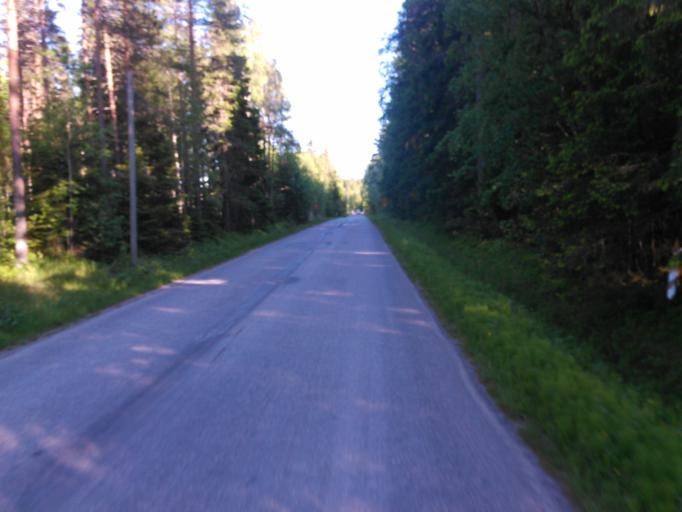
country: SE
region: Vaesterbotten
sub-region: Umea Kommun
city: Ersmark
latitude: 63.8712
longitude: 20.3315
